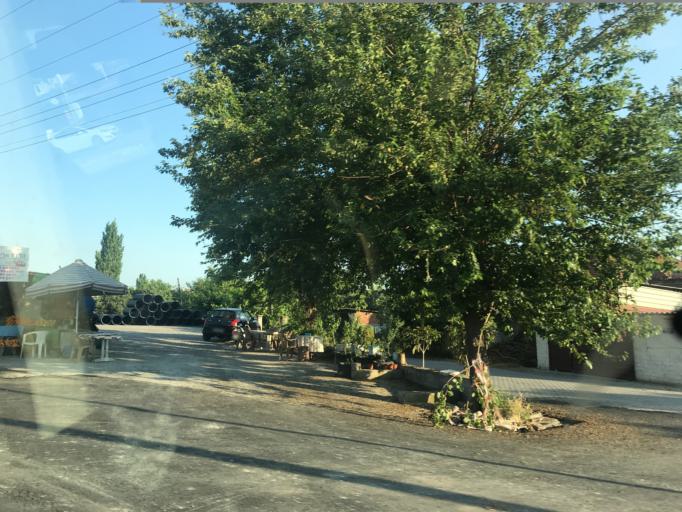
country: TR
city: Dalyan
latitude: 36.9846
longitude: 28.6696
